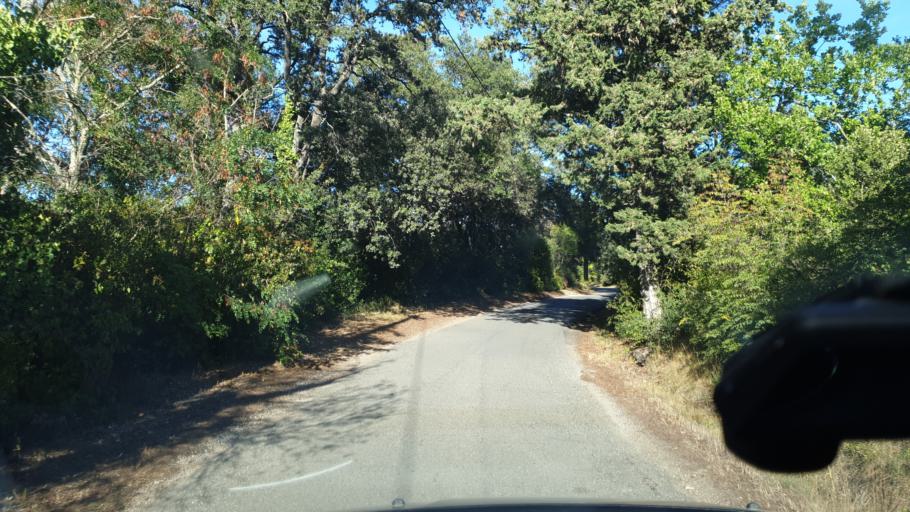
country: FR
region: Provence-Alpes-Cote d'Azur
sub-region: Departement du Vaucluse
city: Monteux
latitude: 44.0492
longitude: 5.0168
